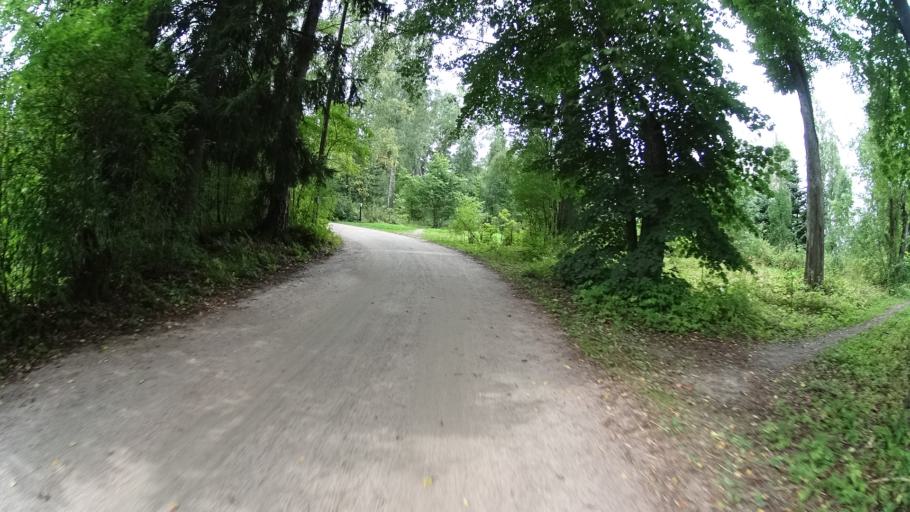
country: FI
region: Uusimaa
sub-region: Helsinki
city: Helsinki
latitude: 60.2736
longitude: 24.9340
